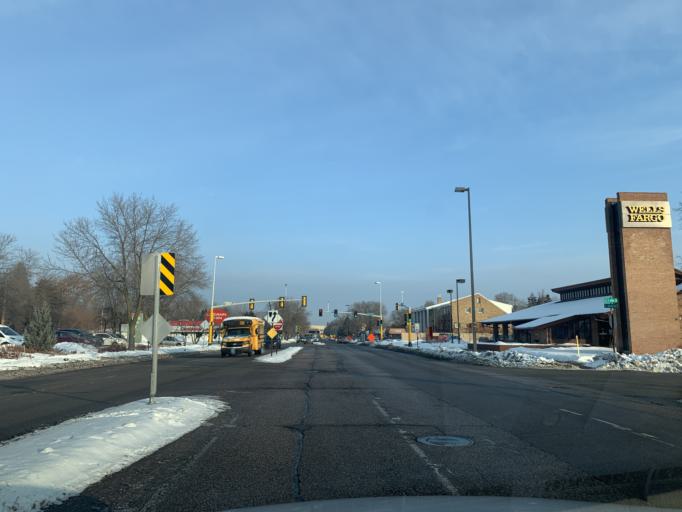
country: US
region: Minnesota
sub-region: Hennepin County
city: Richfield
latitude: 44.8851
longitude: -93.2780
